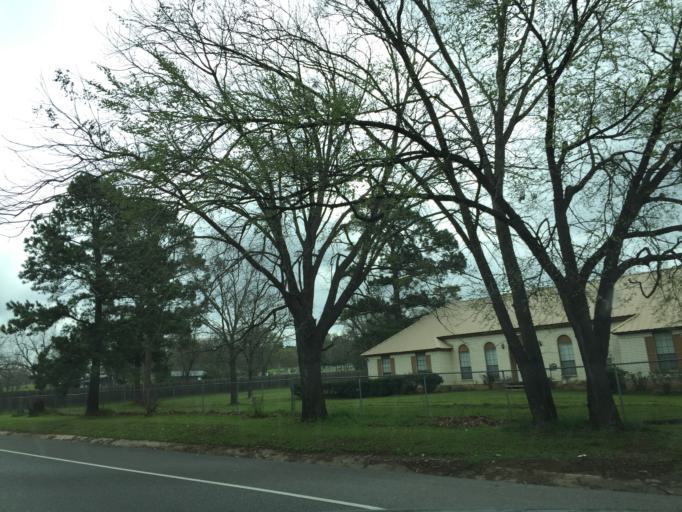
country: US
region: Texas
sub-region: Bastrop County
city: Bastrop
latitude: 30.1129
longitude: -97.3077
